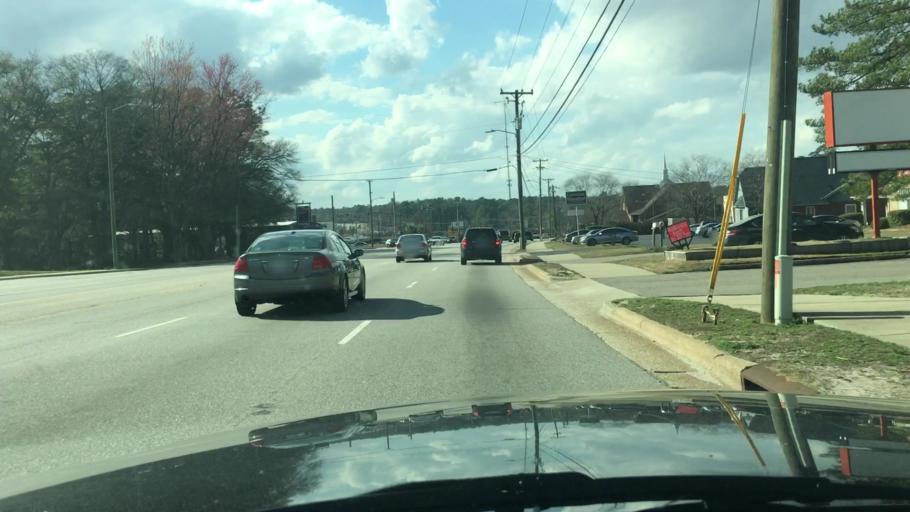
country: US
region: North Carolina
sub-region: Cumberland County
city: Hope Mills
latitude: 35.0432
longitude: -78.9710
